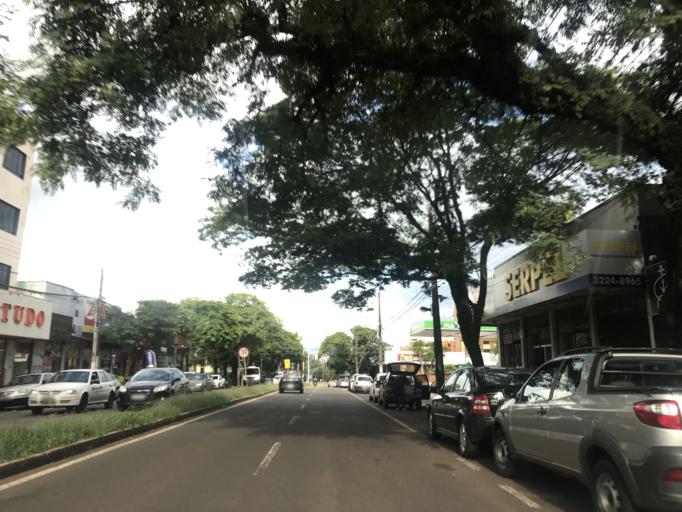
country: BR
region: Parana
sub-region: Maringa
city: Maringa
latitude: -23.4233
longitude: -51.9557
